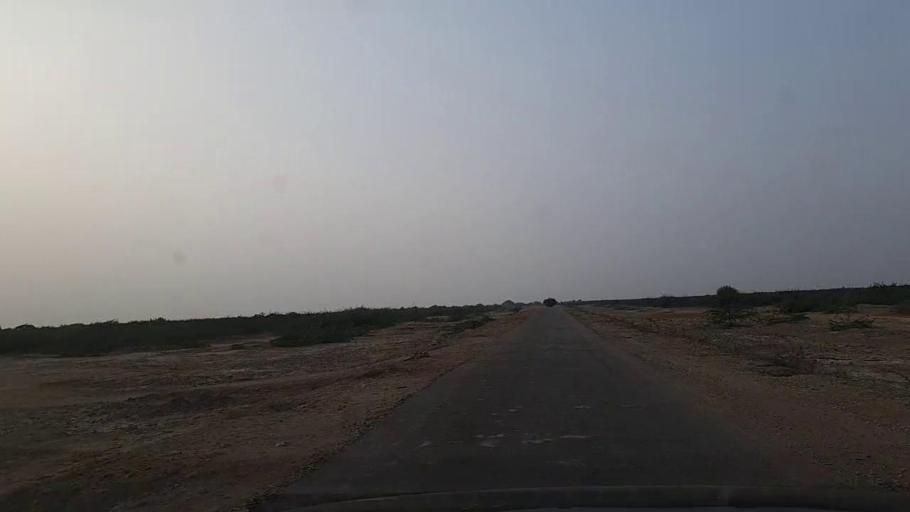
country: PK
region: Sindh
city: Gharo
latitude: 24.7815
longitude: 67.7304
